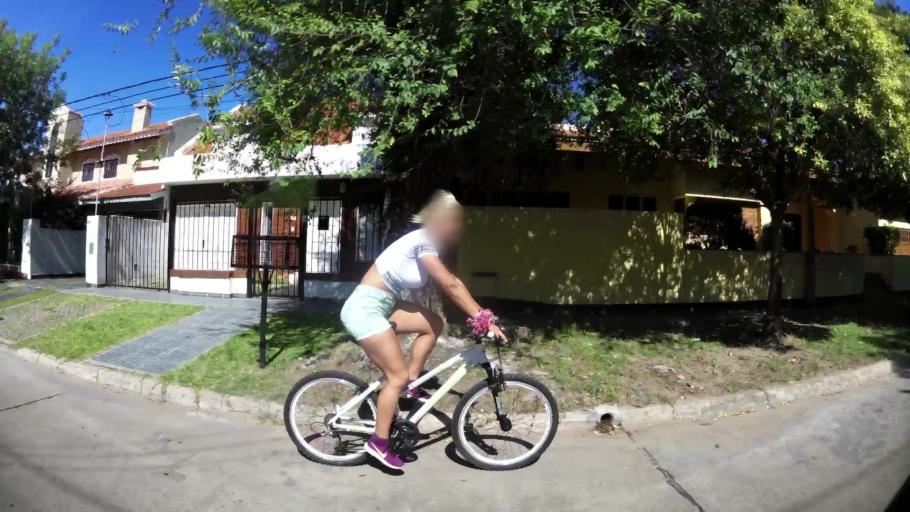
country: AR
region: Santa Fe
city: Santa Fe de la Vera Cruz
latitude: -31.6110
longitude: -60.6719
